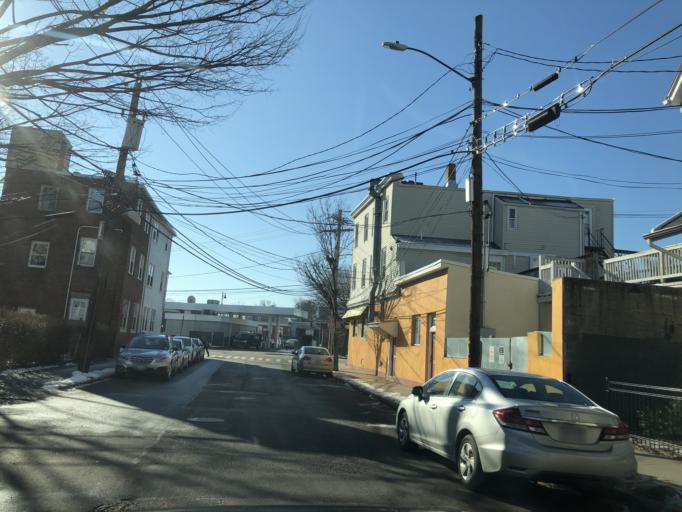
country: US
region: Massachusetts
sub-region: Middlesex County
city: Cambridge
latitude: 42.3866
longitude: -71.1135
